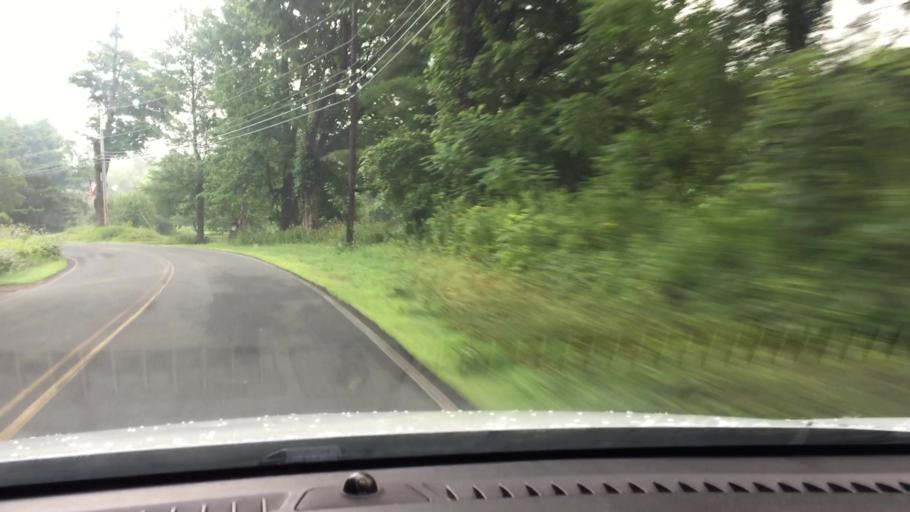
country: US
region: Massachusetts
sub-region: Hampshire County
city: Westhampton
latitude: 42.2446
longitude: -72.9135
